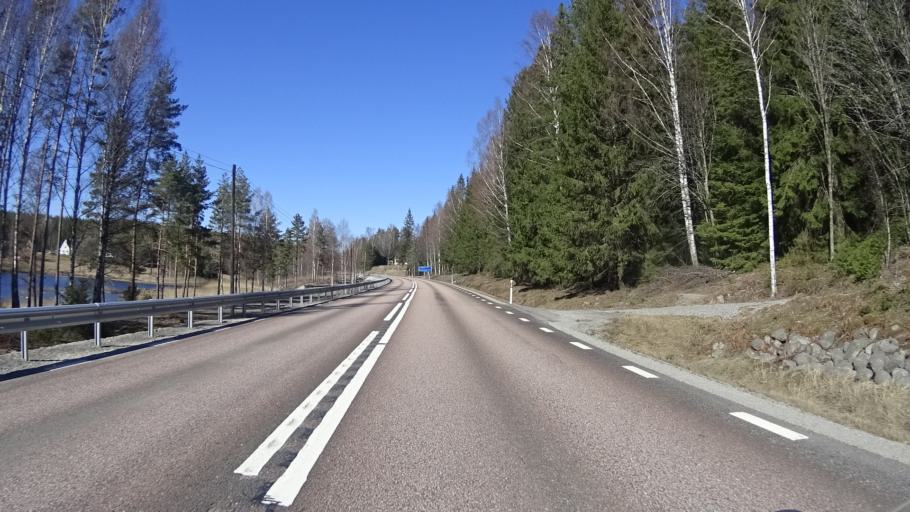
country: SE
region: Vaermland
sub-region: Sunne Kommun
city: Sunne
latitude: 59.6493
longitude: 12.9452
